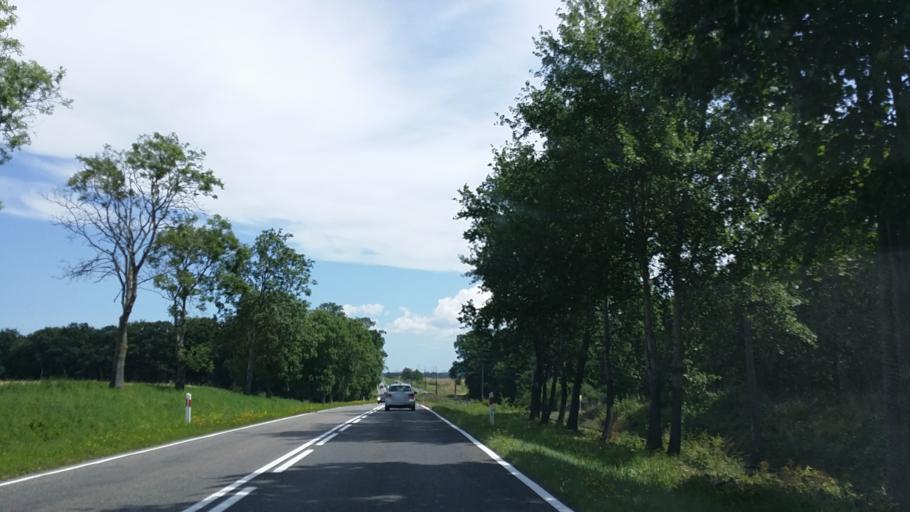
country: PL
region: West Pomeranian Voivodeship
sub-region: Powiat kolobrzeski
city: Ustronie Morskie
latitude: 54.2045
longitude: 15.8144
